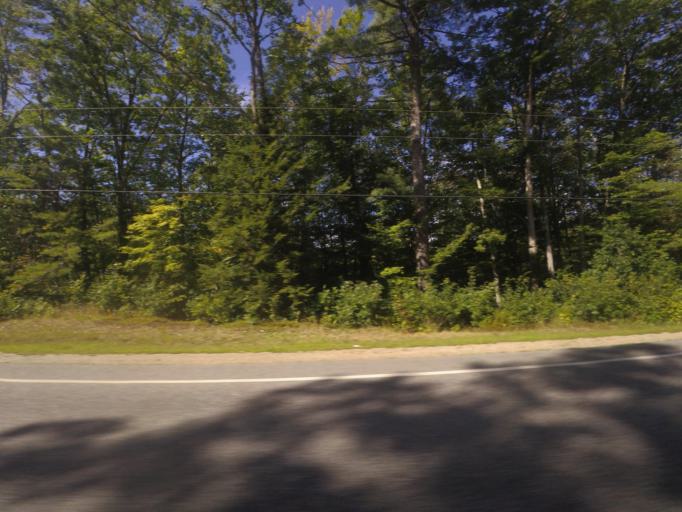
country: US
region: New Hampshire
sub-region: Hillsborough County
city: Antrim
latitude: 43.0768
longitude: -72.0050
